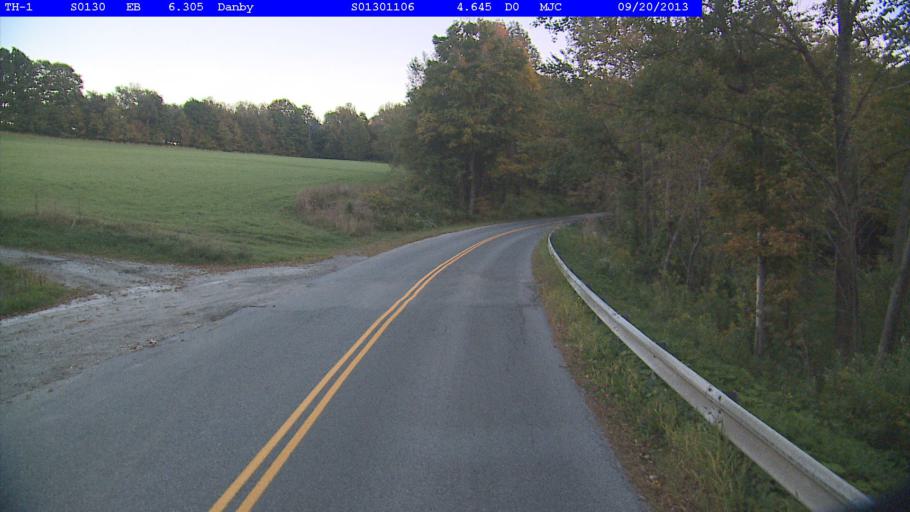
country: US
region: Vermont
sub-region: Bennington County
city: Manchester Center
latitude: 43.3487
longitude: -73.0487
